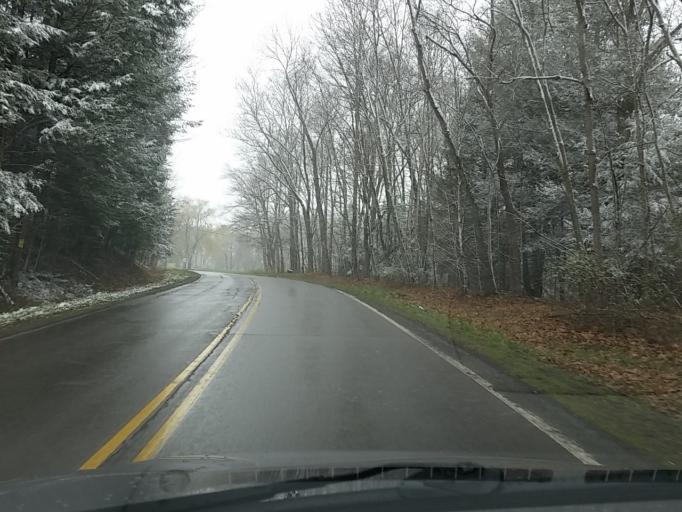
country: US
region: Pennsylvania
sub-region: Luzerne County
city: Glen Lyon
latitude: 41.2010
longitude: -76.1878
